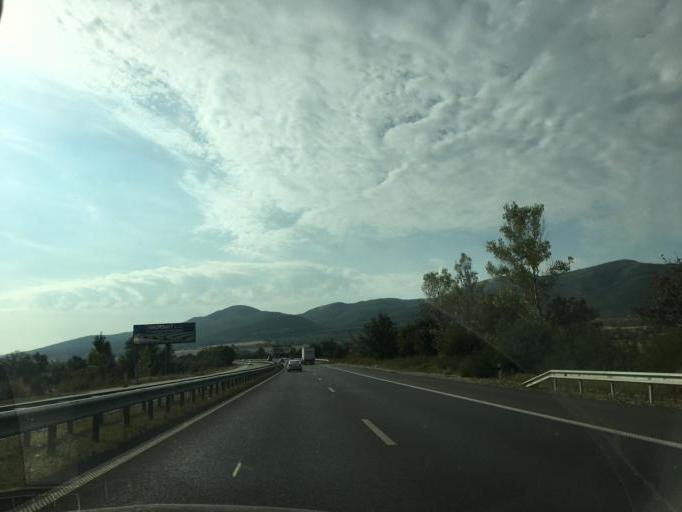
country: BG
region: Sofiya
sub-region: Obshtina Elin Pelin
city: Elin Pelin
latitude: 42.6190
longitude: 23.5233
